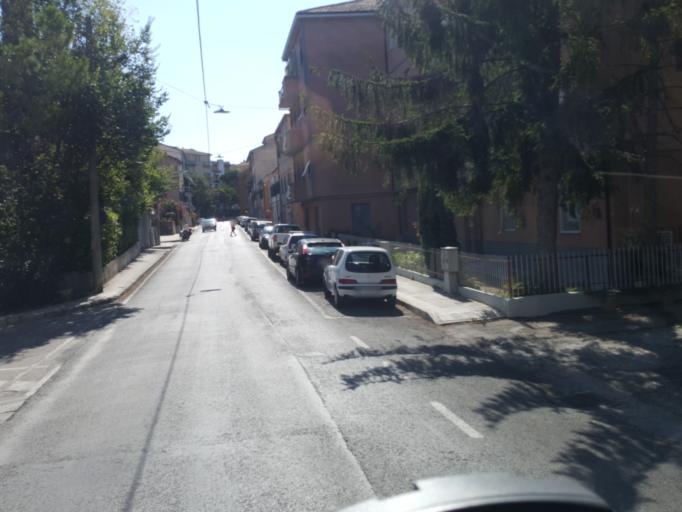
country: IT
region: The Marches
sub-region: Provincia di Ancona
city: Le Grazie di Ancona
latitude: 43.6023
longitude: 13.5137
